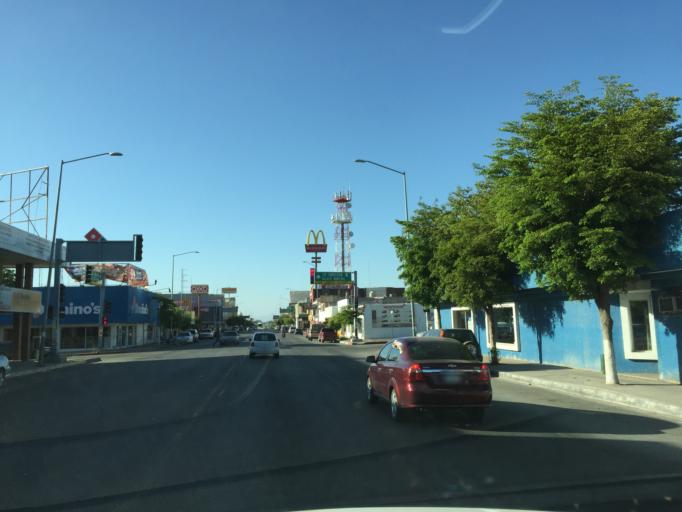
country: MX
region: Sonora
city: Navojoa
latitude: 27.0778
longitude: -109.4444
